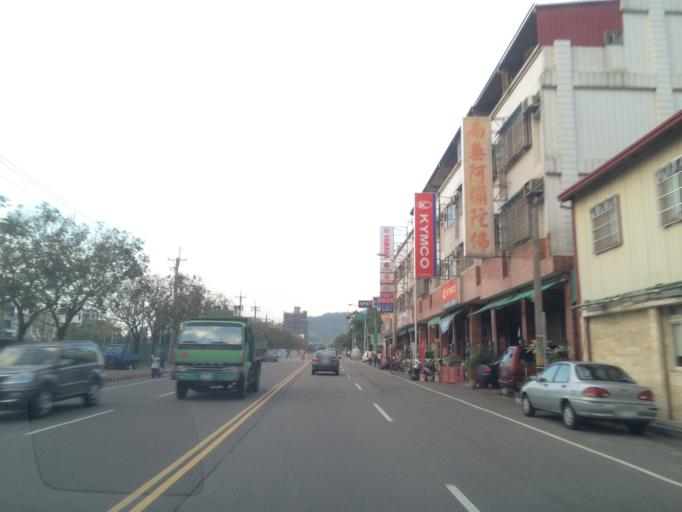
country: TW
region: Taiwan
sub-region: Taichung City
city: Taichung
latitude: 24.1636
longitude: 120.7334
